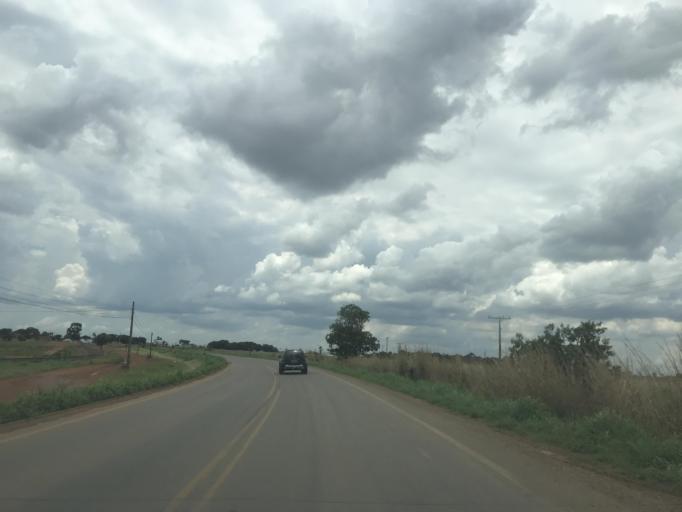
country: BR
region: Goias
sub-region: Vianopolis
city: Vianopolis
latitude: -16.7377
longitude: -48.5008
